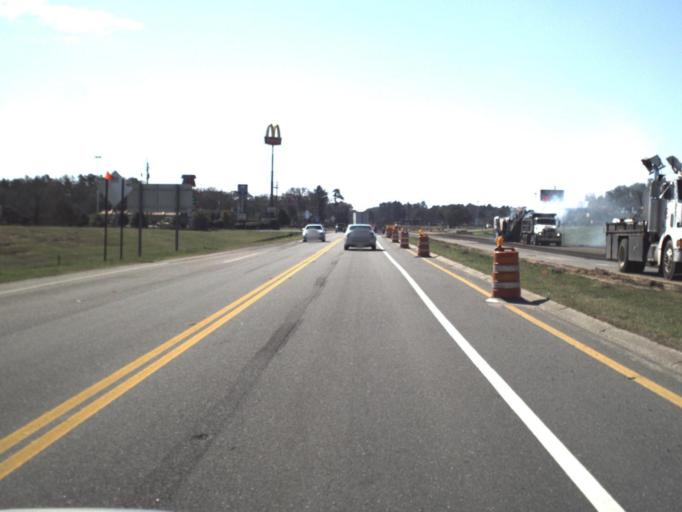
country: US
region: Florida
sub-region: Jackson County
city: Marianna
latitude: 30.7196
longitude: -85.1854
